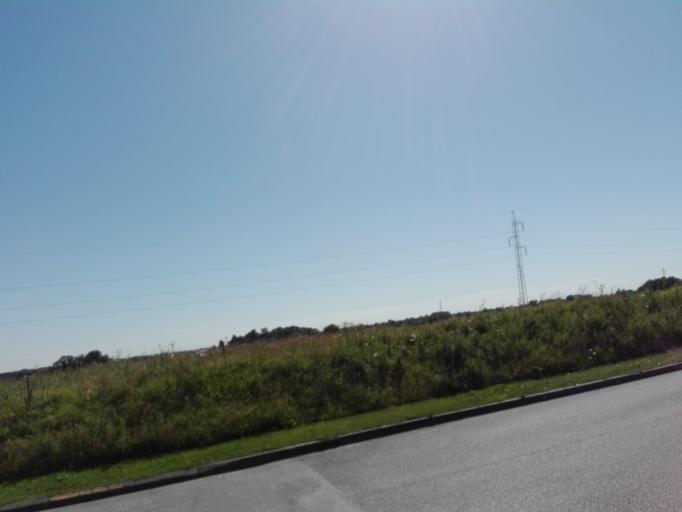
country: DK
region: Central Jutland
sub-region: Arhus Kommune
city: Tranbjerg
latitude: 56.1026
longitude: 10.1475
